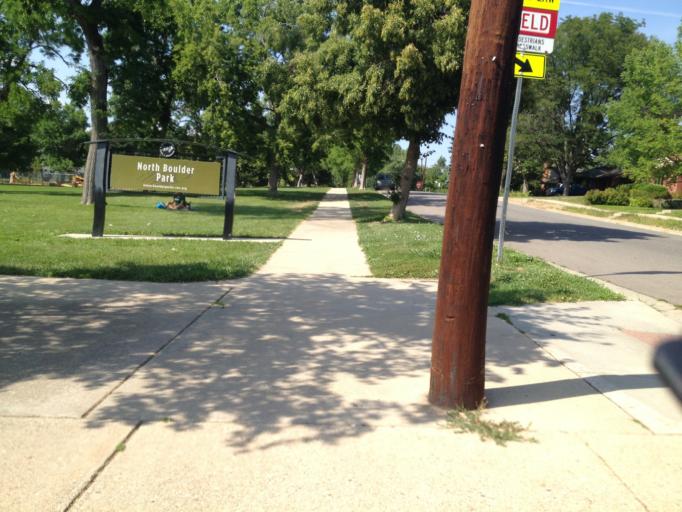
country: US
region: Colorado
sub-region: Boulder County
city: Boulder
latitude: 40.0280
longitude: -105.2857
